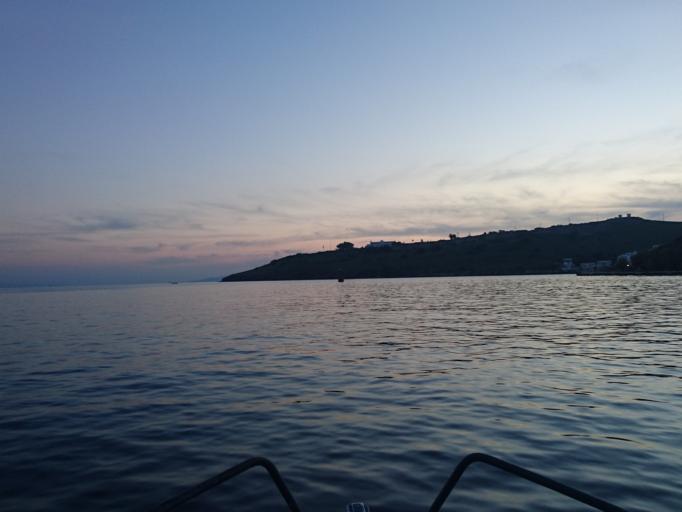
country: TR
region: Mugla
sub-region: Bodrum
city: Bodrum
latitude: 37.0307
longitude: 27.4237
